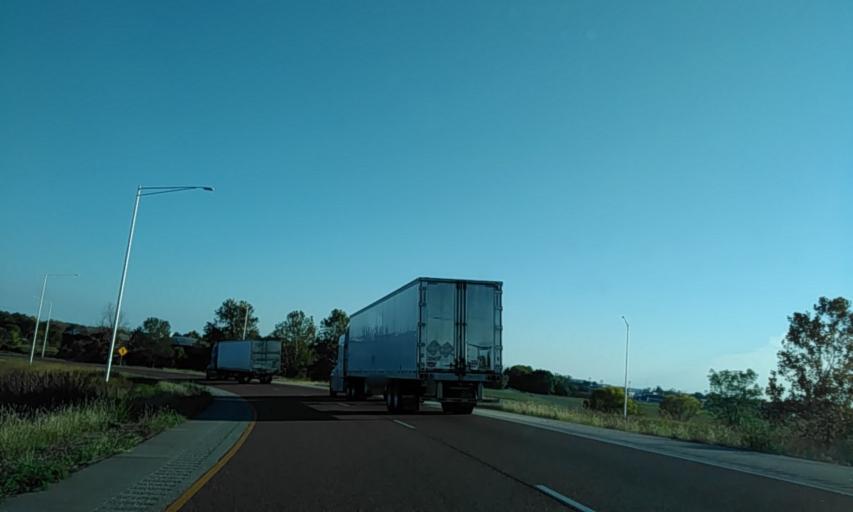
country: US
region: Illinois
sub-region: Saint Clair County
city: Caseyville
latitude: 38.6712
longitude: -90.0331
